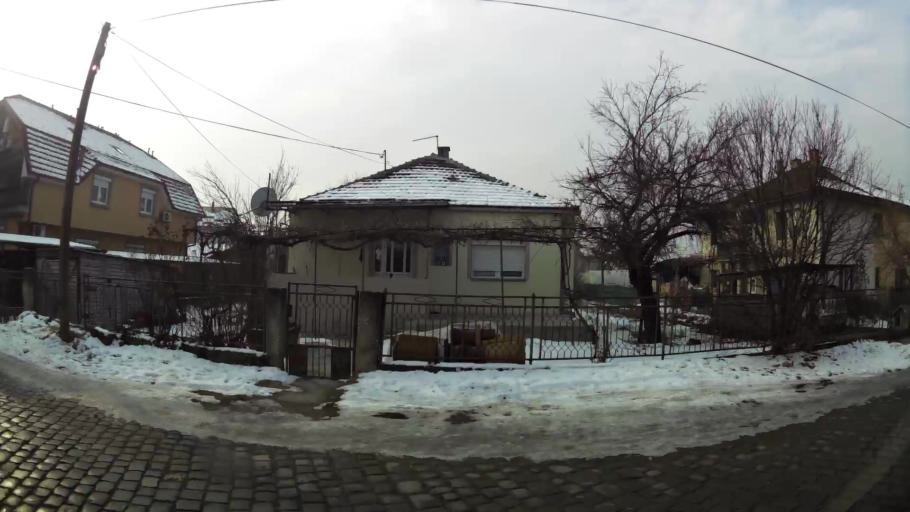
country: MK
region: Kisela Voda
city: Kisela Voda
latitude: 41.9967
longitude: 21.5032
